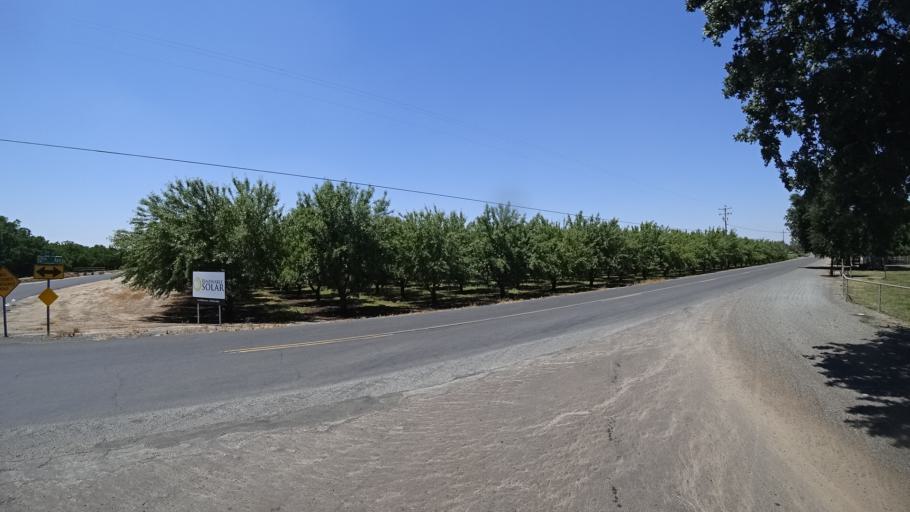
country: US
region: California
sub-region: Fresno County
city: Laton
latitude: 36.4159
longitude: -119.6727
